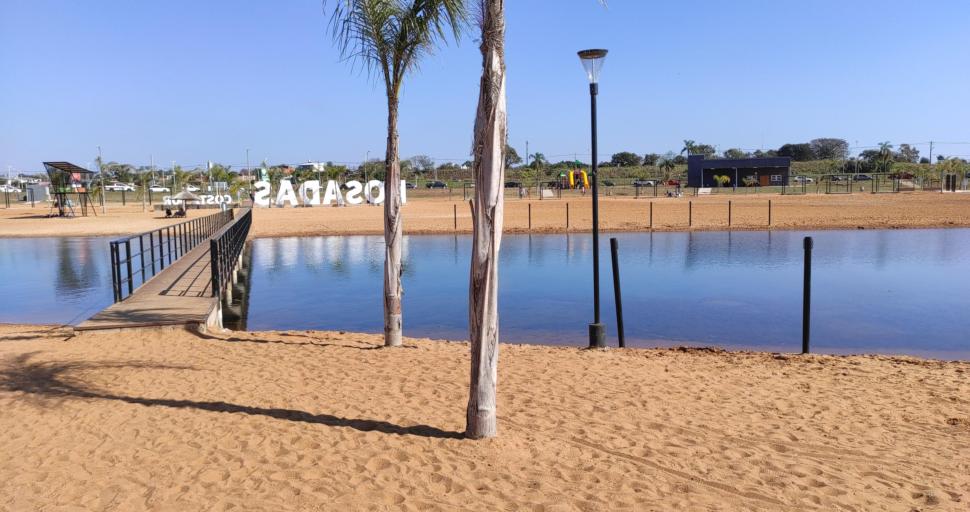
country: AR
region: Misiones
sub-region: Departamento de Capital
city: Posadas
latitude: -27.4194
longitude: -55.8768
